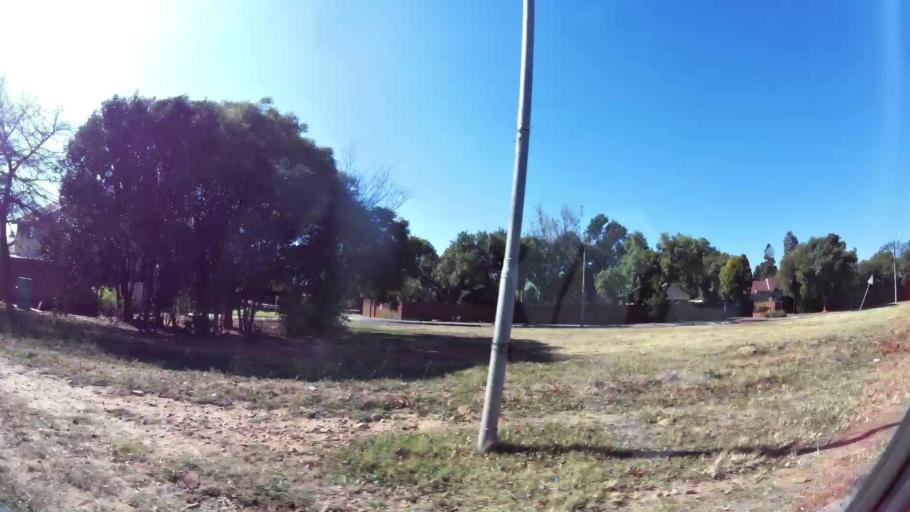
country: ZA
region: Gauteng
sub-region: City of Johannesburg Metropolitan Municipality
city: Roodepoort
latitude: -26.1448
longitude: 27.9018
